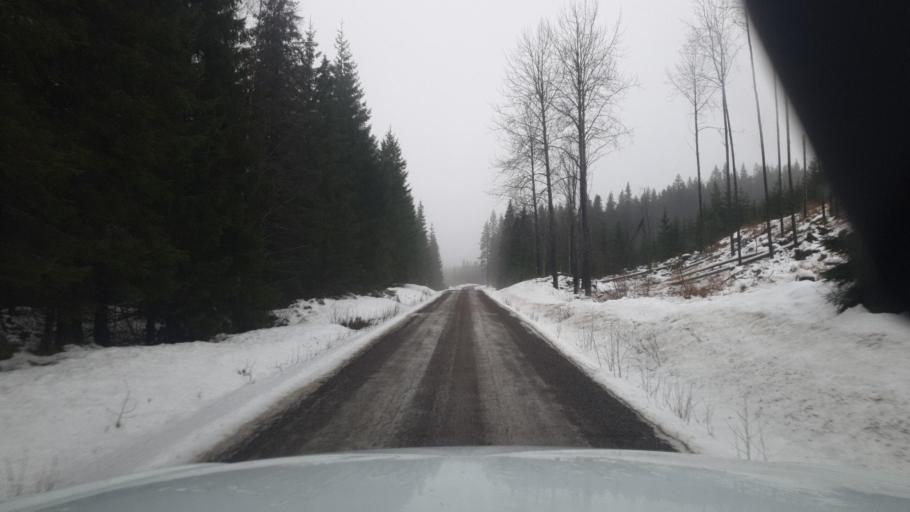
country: SE
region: Vaermland
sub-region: Eda Kommun
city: Charlottenberg
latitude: 60.0444
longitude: 12.6307
